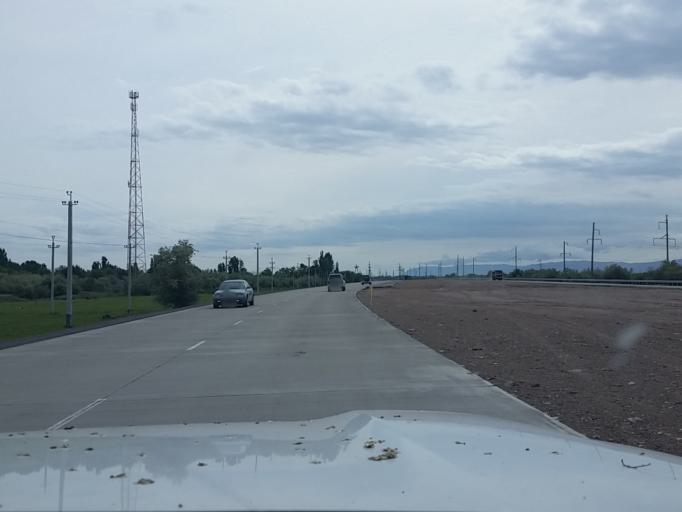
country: KZ
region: Almaty Oblysy
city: Turgen'
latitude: 43.5835
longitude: 78.2439
